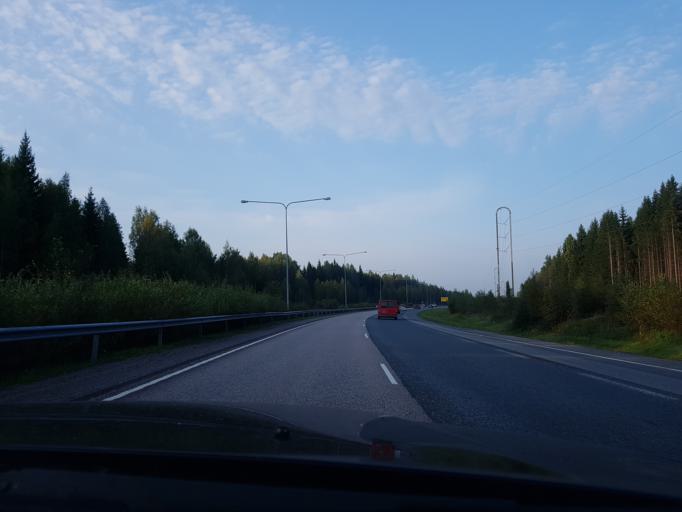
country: FI
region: Uusimaa
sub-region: Helsinki
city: Tuusula
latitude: 60.3604
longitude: 25.0016
